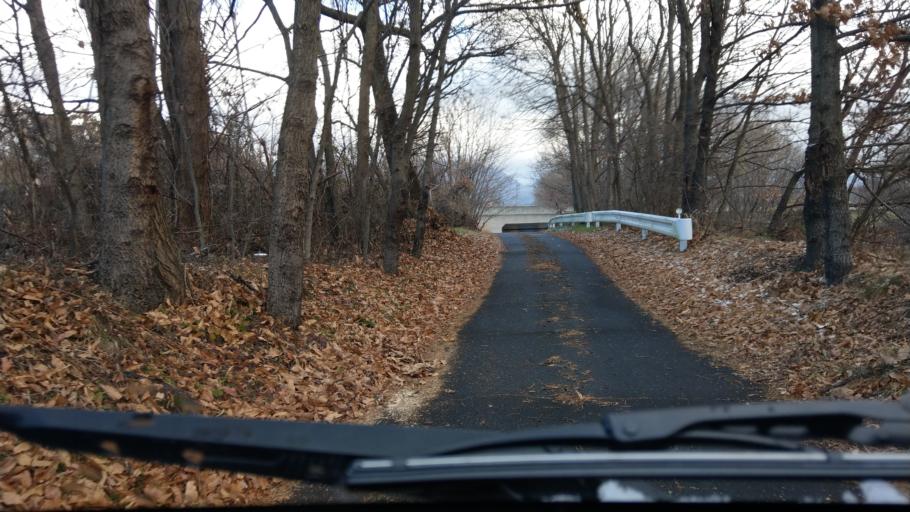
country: JP
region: Nagano
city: Komoro
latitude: 36.3464
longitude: 138.3970
